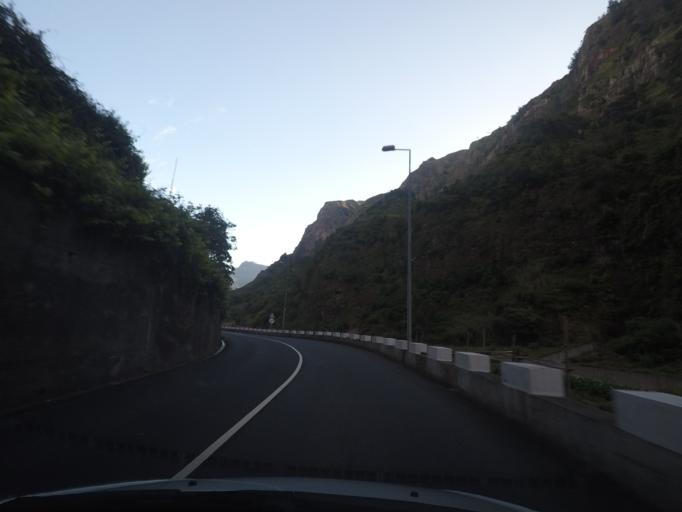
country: PT
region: Madeira
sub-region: Ribeira Brava
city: Campanario
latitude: 32.7071
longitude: -17.0369
